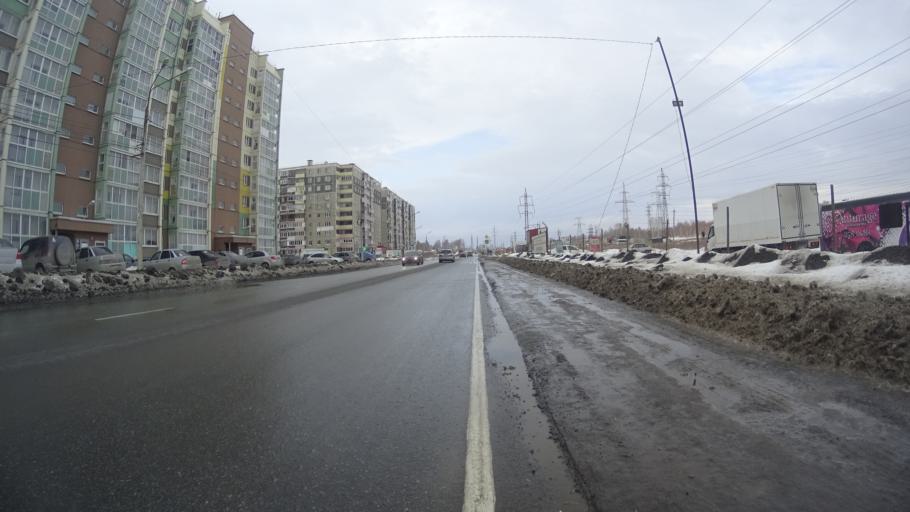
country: RU
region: Chelyabinsk
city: Roshchino
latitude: 55.2175
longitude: 61.3009
